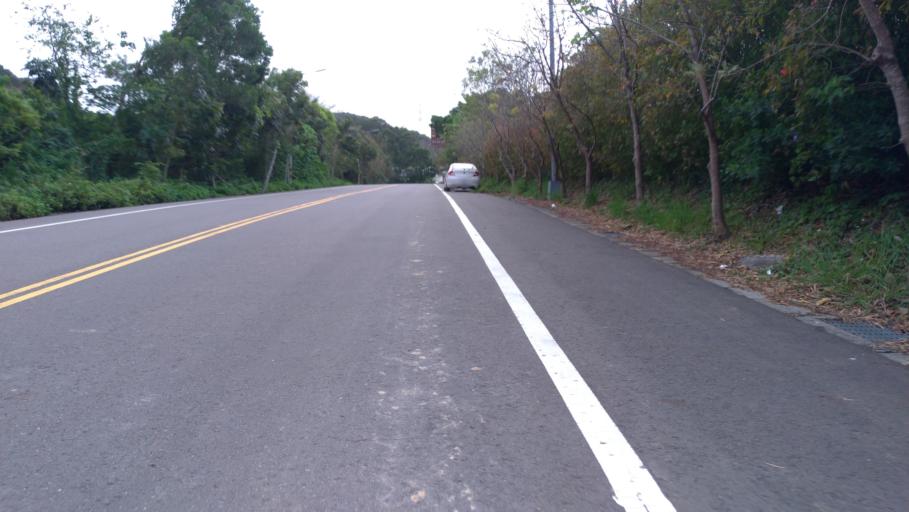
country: TW
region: Taiwan
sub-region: Hsinchu
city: Hsinchu
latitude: 24.7605
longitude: 120.9843
